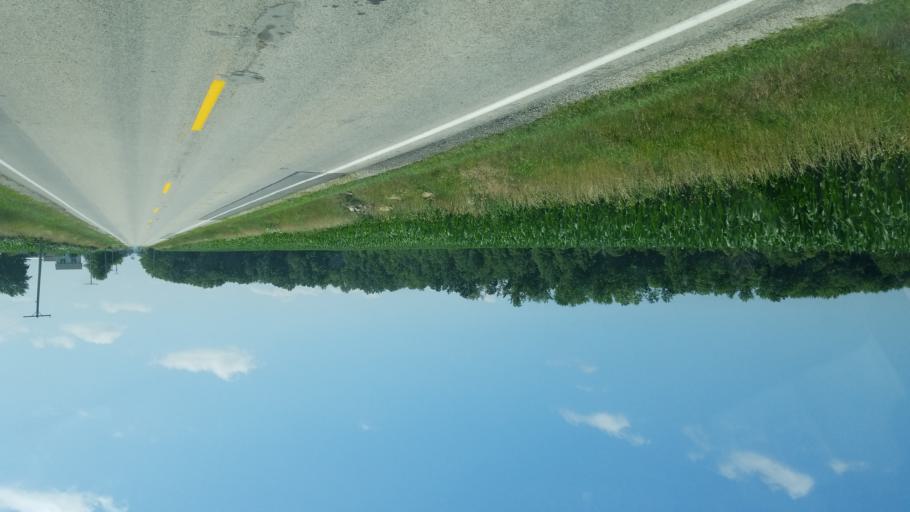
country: US
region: Ohio
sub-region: Huron County
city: Bellevue
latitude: 41.1992
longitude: -82.8378
